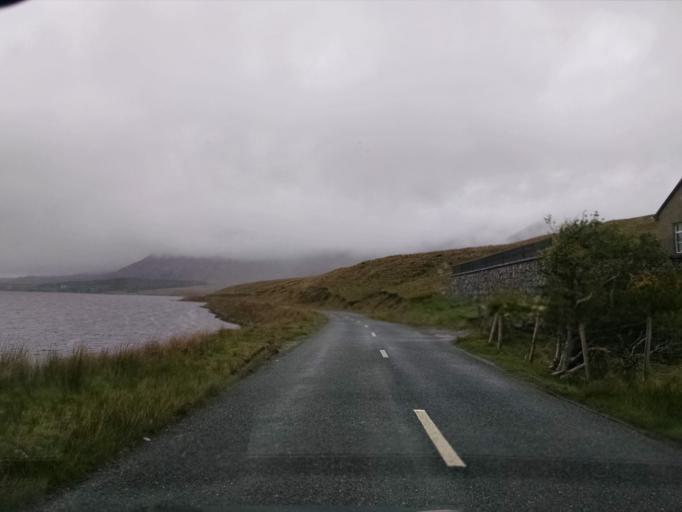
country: IE
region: Connaught
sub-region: County Galway
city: Clifden
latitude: 53.4965
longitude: -9.7350
